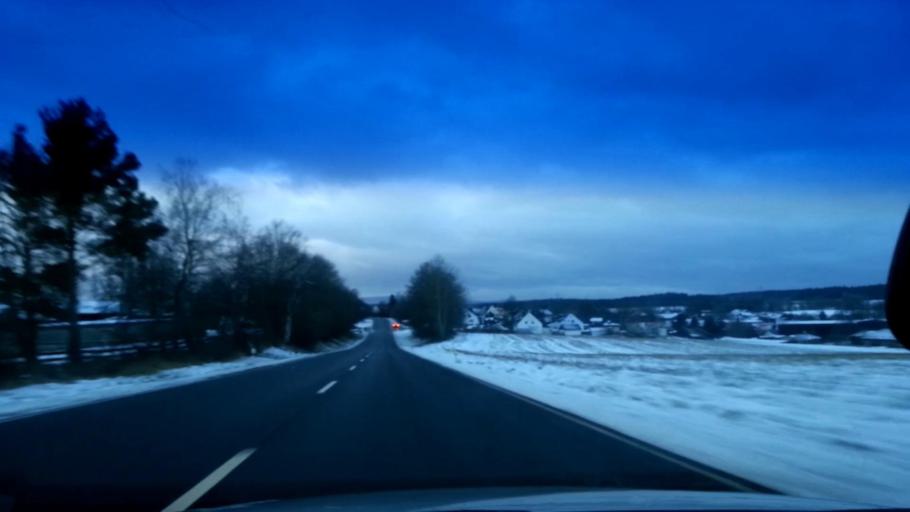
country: DE
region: Bavaria
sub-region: Upper Franconia
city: Marktleuthen
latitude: 50.1483
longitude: 12.0232
